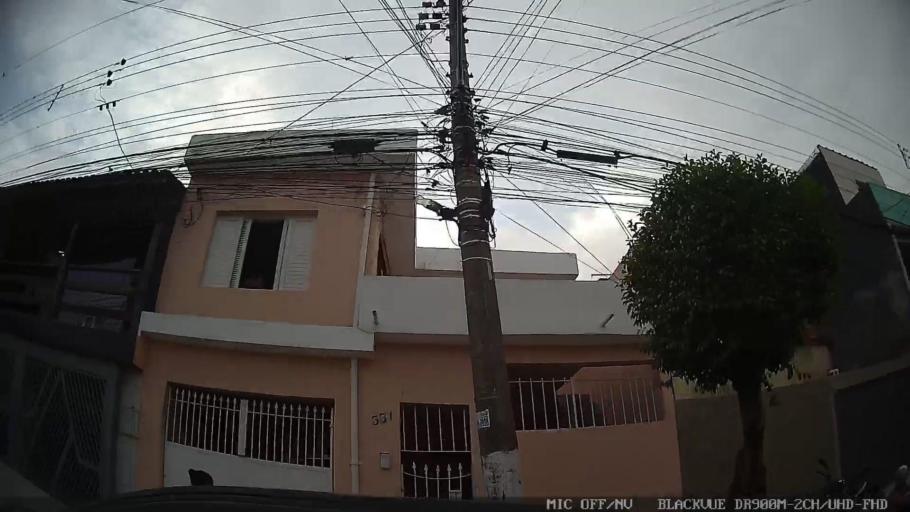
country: BR
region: Sao Paulo
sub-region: Itaquaquecetuba
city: Itaquaquecetuba
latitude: -23.4900
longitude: -46.4142
